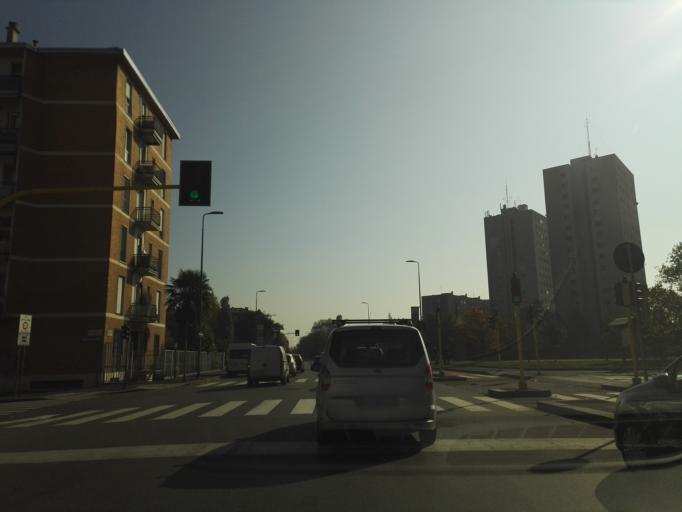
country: IT
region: Lombardy
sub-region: Citta metropolitana di Milano
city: Chiaravalle
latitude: 45.4346
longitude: 9.2191
